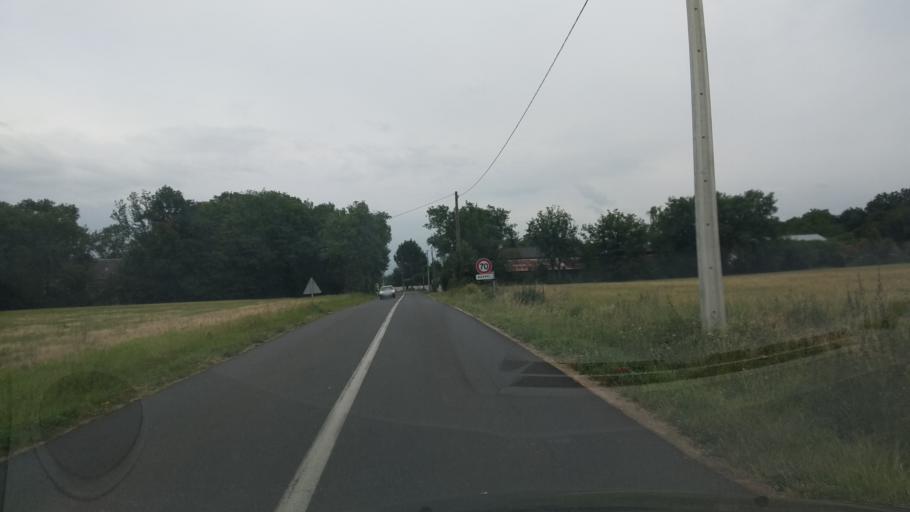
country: FR
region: Poitou-Charentes
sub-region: Departement de la Vienne
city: Vouneuil-sous-Biard
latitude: 46.5843
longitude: 0.2843
